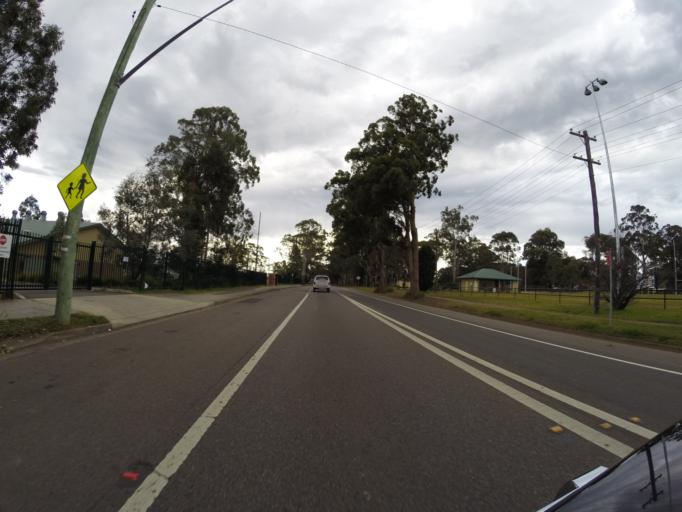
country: AU
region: New South Wales
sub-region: Wollondilly
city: Douglas Park
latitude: -34.1988
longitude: 150.7883
